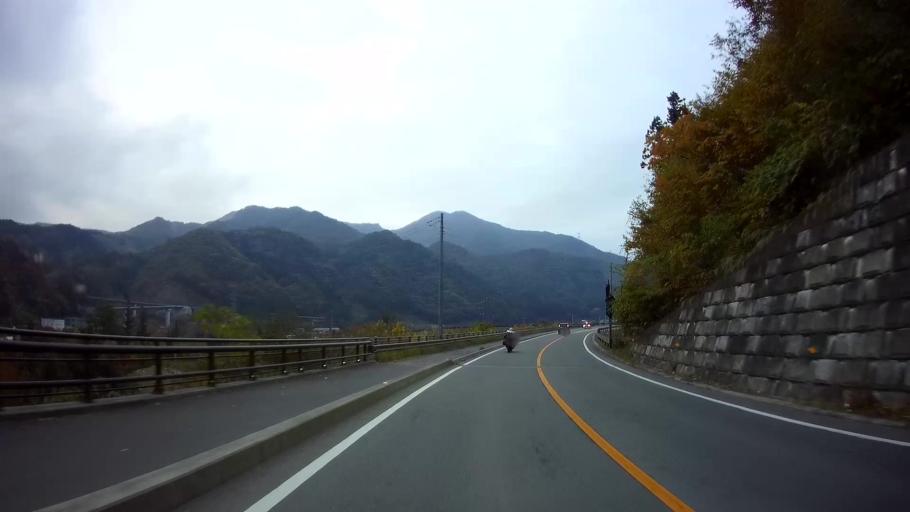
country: JP
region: Gunma
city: Nakanojomachi
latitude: 36.5677
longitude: 138.7319
